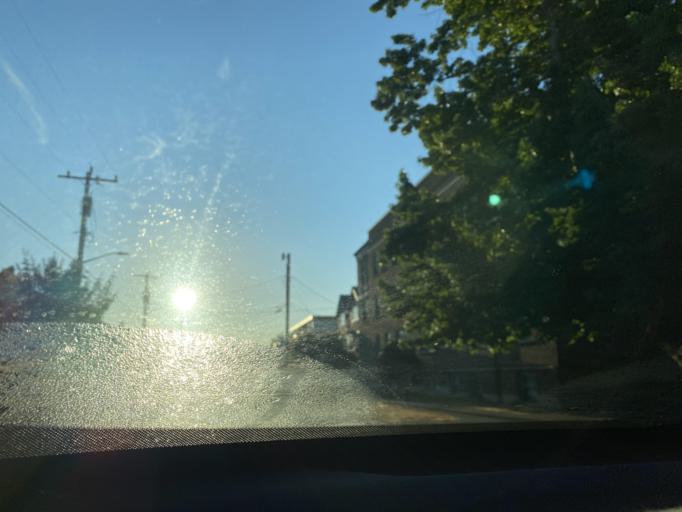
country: US
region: Washington
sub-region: King County
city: Seattle
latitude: 47.6717
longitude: -122.3836
